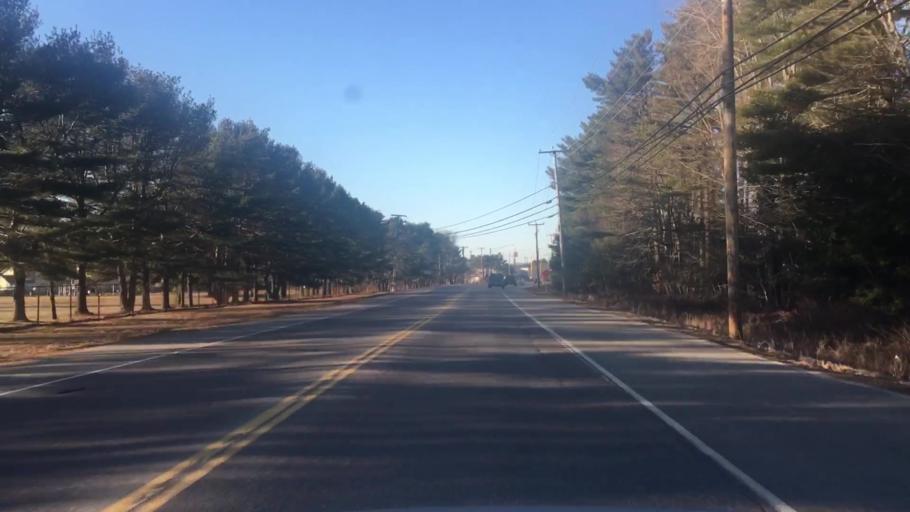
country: US
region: Maine
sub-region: Cumberland County
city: Brunswick
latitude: 43.9011
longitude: -69.9116
